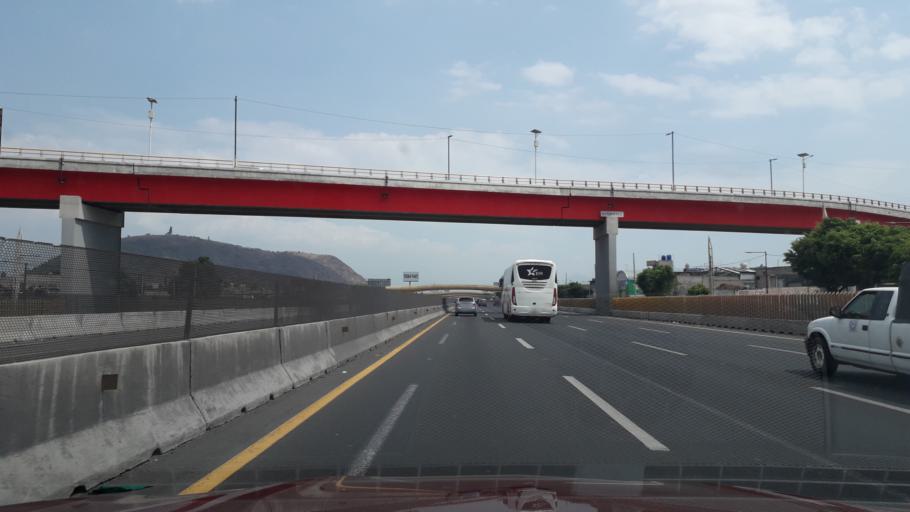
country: MX
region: Mexico
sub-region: La Paz
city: San Isidro
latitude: 19.3068
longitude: -98.9386
